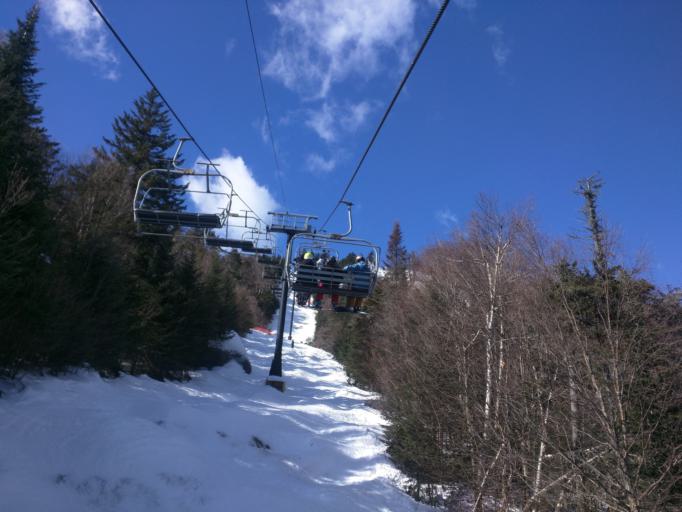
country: US
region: New York
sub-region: Warren County
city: Warrensburg
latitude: 43.6715
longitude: -74.0424
